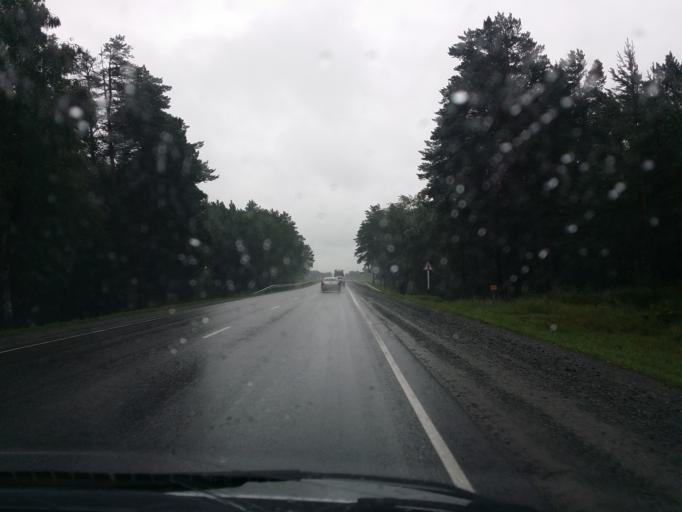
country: RU
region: Altai Krai
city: Bayunovskiye Klyuchi
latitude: 53.3183
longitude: 84.2066
